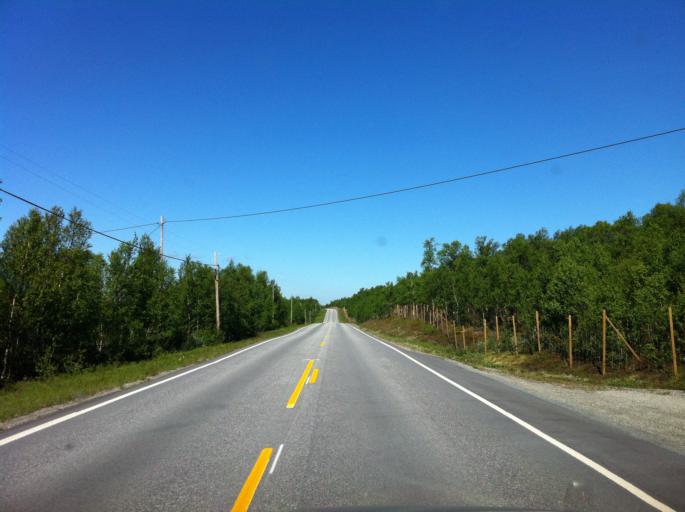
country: NO
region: Sor-Trondelag
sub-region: Tydal
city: Aas
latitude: 62.6354
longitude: 11.9280
